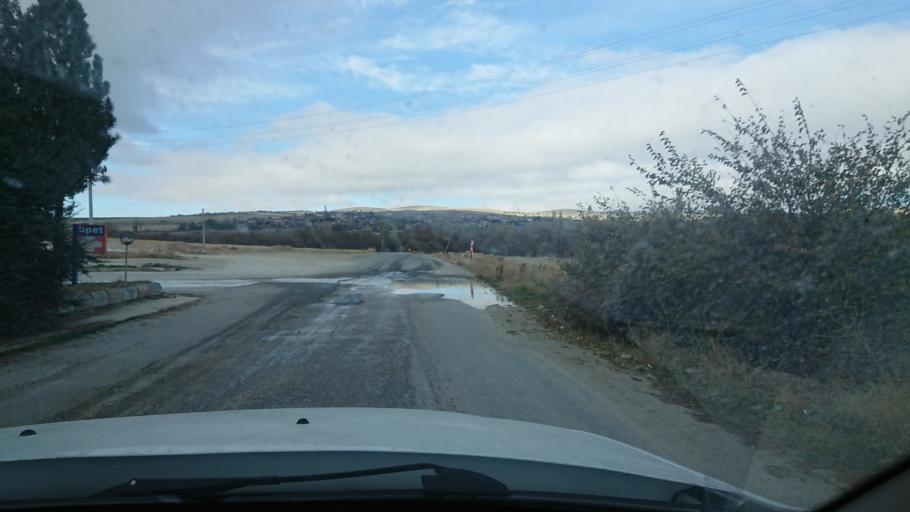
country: TR
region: Aksaray
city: Ortakoy
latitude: 38.7519
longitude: 34.0229
